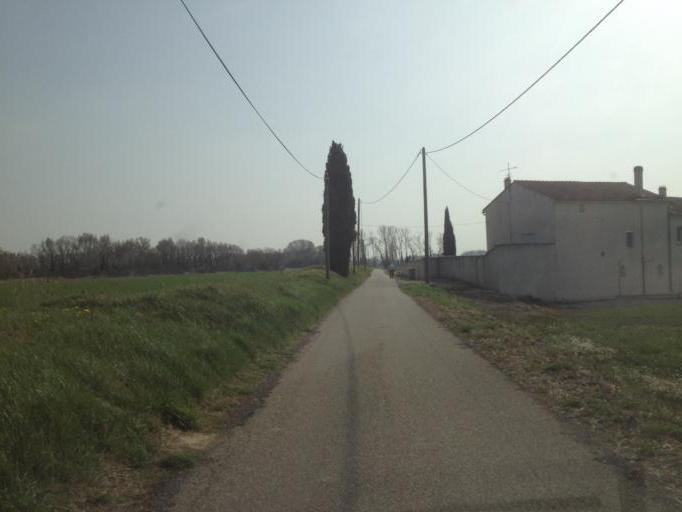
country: FR
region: Provence-Alpes-Cote d'Azur
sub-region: Departement du Vaucluse
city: Bedarrides
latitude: 44.0613
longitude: 4.9286
